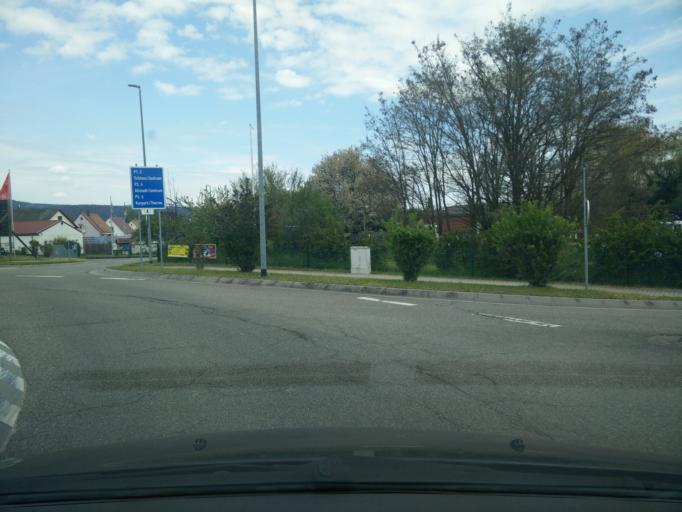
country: DE
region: Rheinland-Pfalz
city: Bad Bergzabern
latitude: 49.0946
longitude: 8.0044
